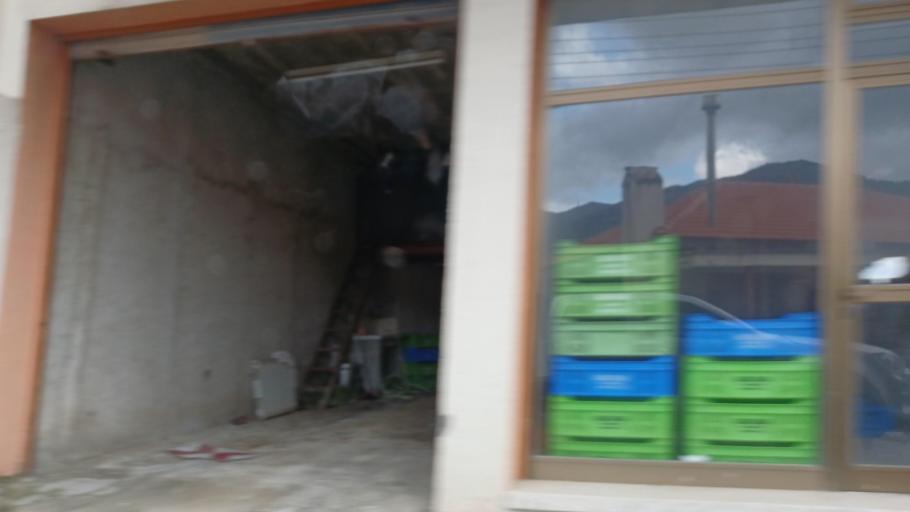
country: CY
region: Limassol
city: Kyperounta
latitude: 34.9381
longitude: 32.9758
